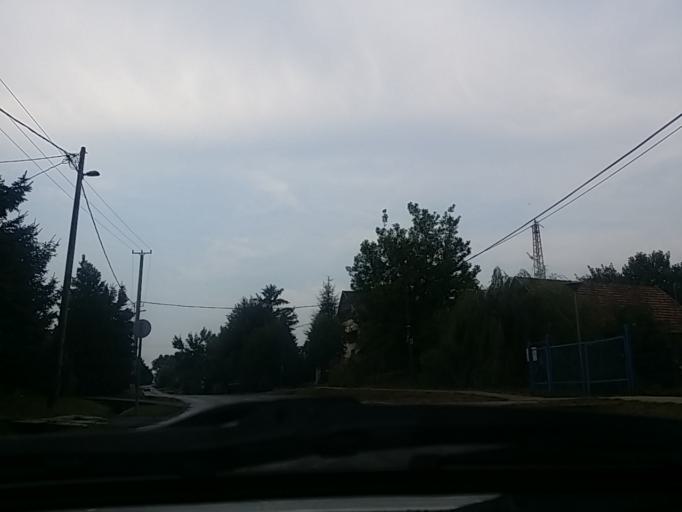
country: HU
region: Pest
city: Paty
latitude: 47.5129
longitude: 18.8190
